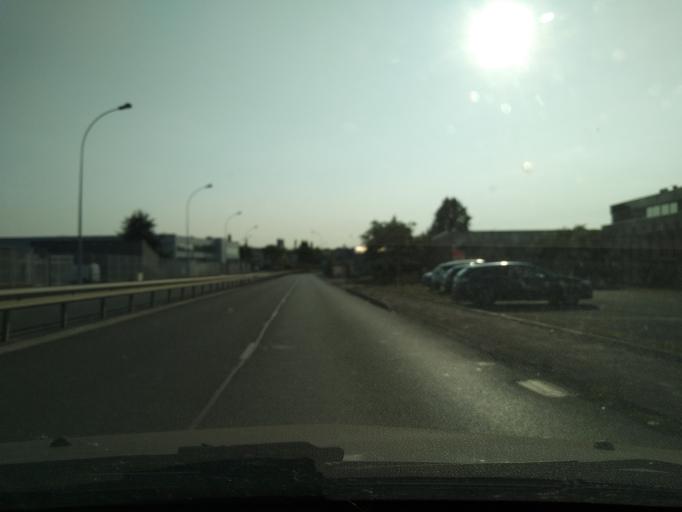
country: FR
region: Centre
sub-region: Departement d'Indre-et-Loire
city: Saint-Cyr-sur-Loire
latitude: 47.4311
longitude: 0.6890
